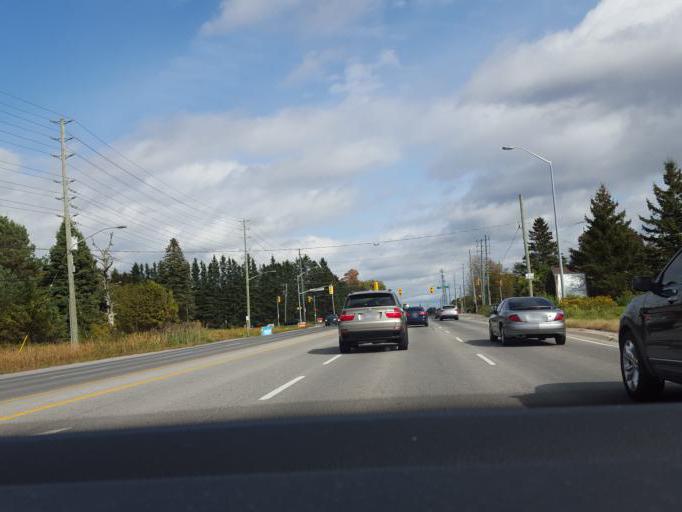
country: CA
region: Ontario
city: Ajax
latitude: 43.9023
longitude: -79.0128
